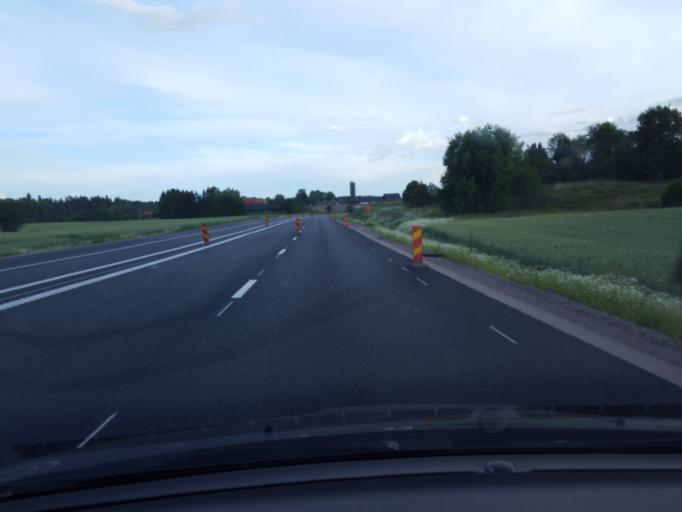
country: SE
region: Uppsala
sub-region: Osthammars Kommun
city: Gimo
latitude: 60.0889
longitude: 18.1206
